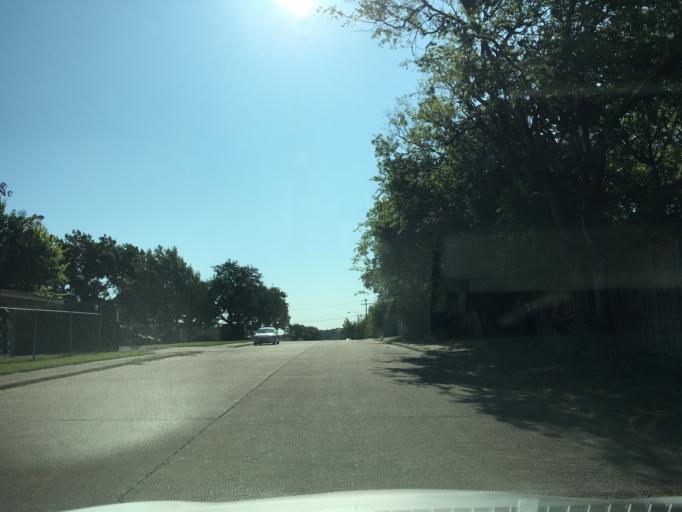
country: US
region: Texas
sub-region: Dallas County
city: Garland
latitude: 32.8635
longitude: -96.7054
